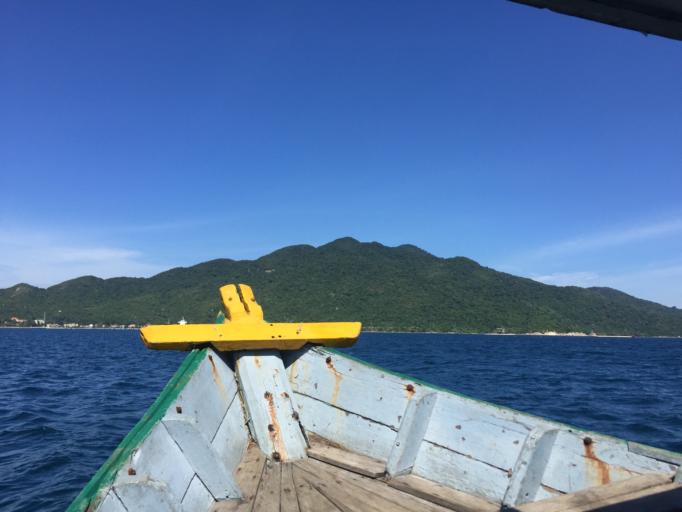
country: VN
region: Quang Nam
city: Hoi An
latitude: 15.9455
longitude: 108.4920
